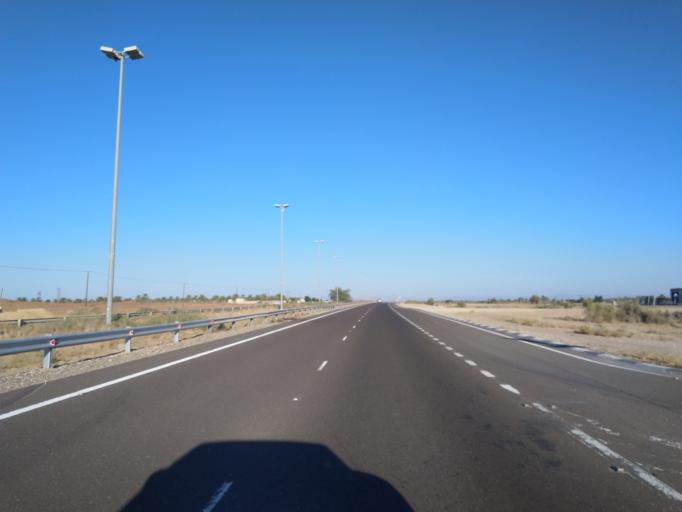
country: OM
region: Al Buraimi
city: Al Buraymi
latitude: 24.5409
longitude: 55.6346
